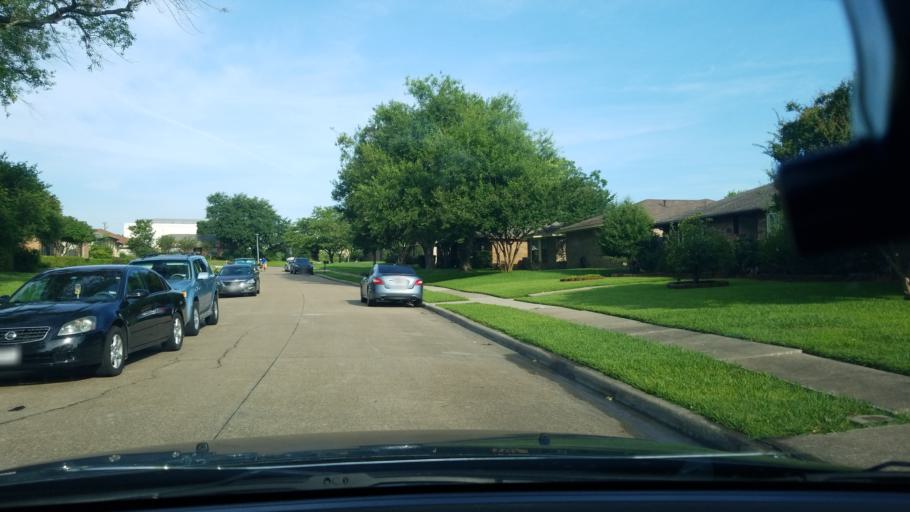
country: US
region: Texas
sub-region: Dallas County
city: Mesquite
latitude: 32.8099
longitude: -96.6068
